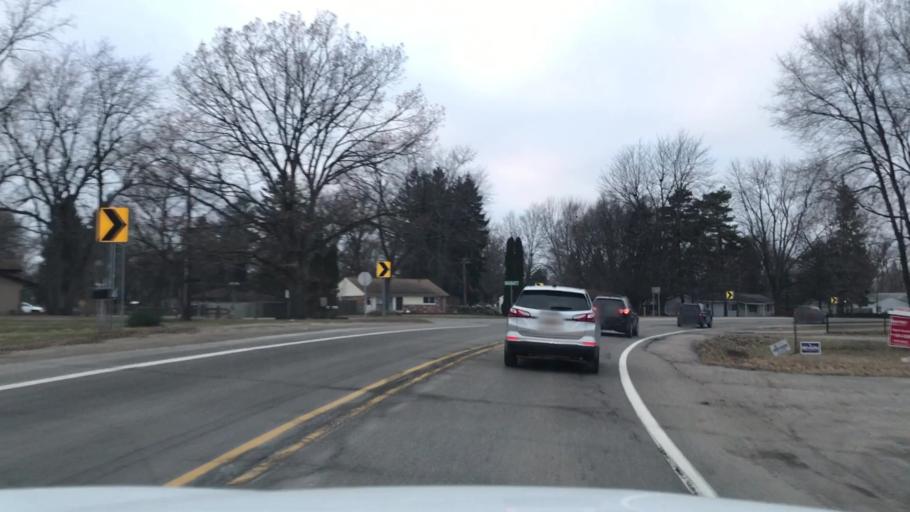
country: US
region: Michigan
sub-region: Oakland County
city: Waterford
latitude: 42.7079
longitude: -83.3778
